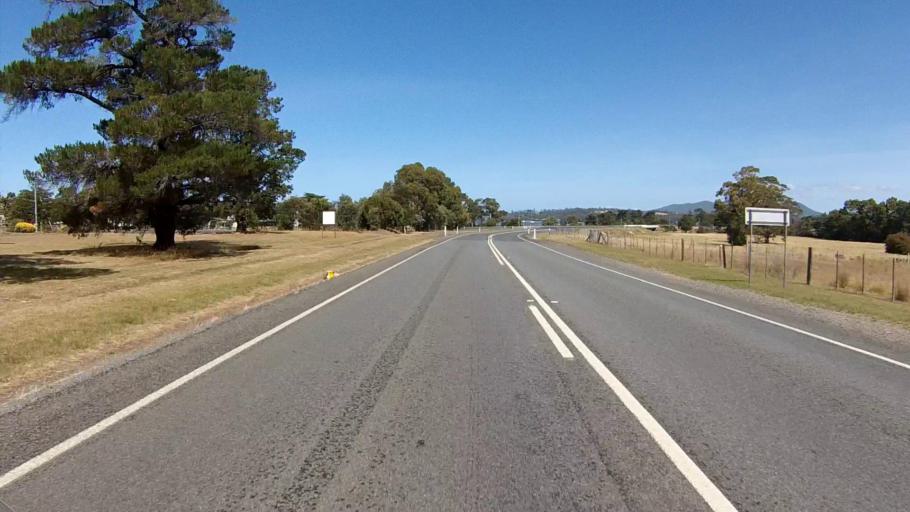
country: AU
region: Tasmania
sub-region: Sorell
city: Sorell
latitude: -42.5059
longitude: 147.9085
